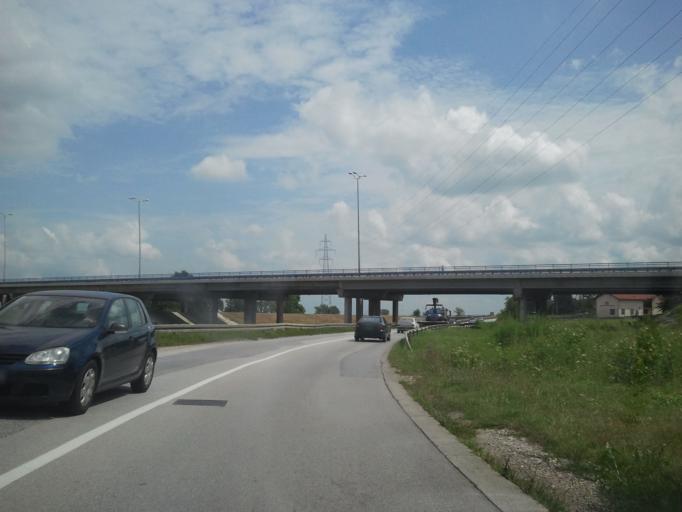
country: HR
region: Grad Zagreb
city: Jankomir
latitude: 45.7617
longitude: 15.9042
